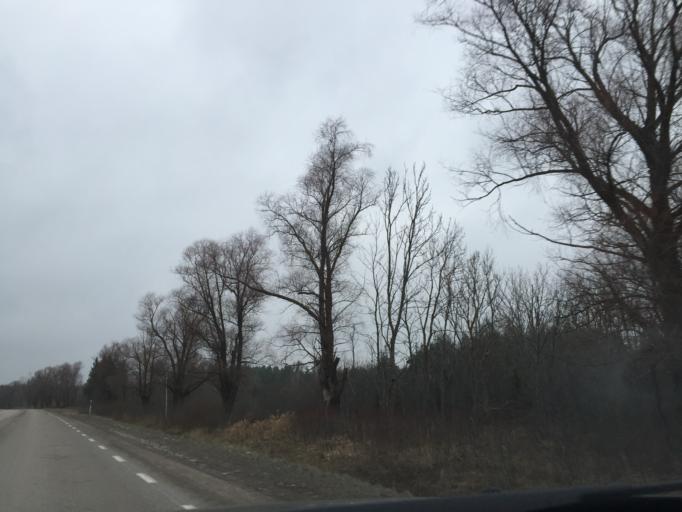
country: EE
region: Saare
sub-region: Kuressaare linn
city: Kuressaare
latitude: 58.2731
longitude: 22.4562
